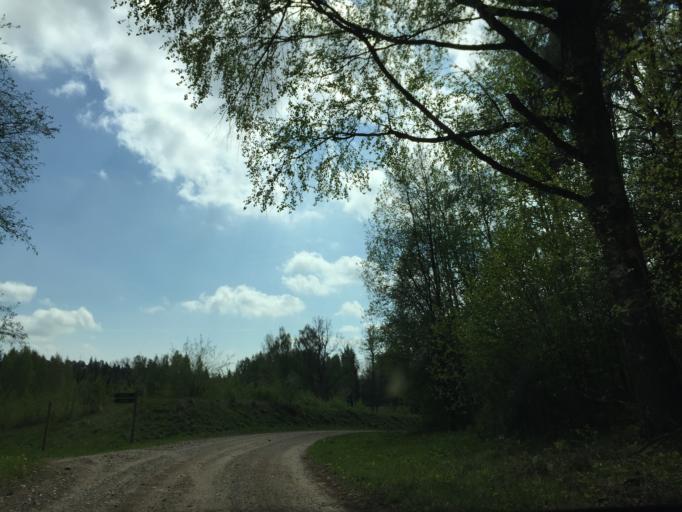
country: LV
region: Ligatne
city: Ligatne
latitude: 57.2899
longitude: 24.9398
